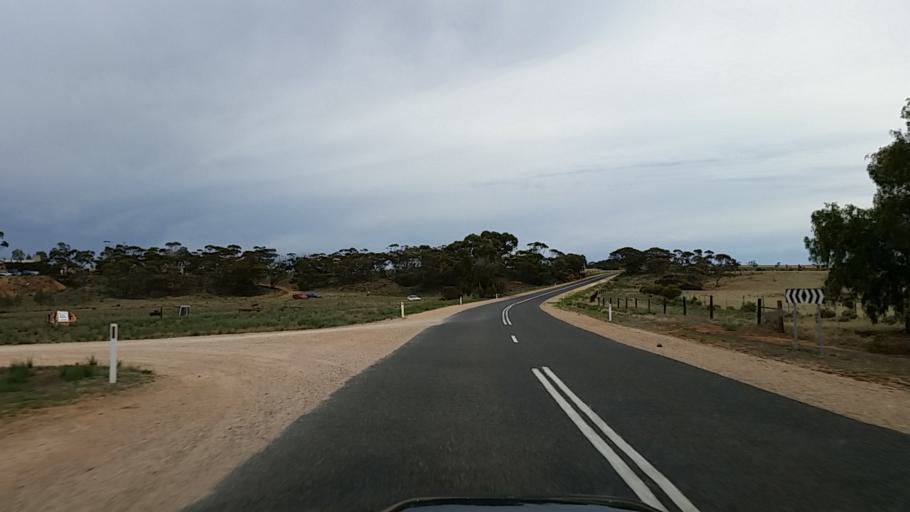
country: AU
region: South Australia
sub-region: Mid Murray
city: Mannum
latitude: -34.7551
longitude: 139.3065
